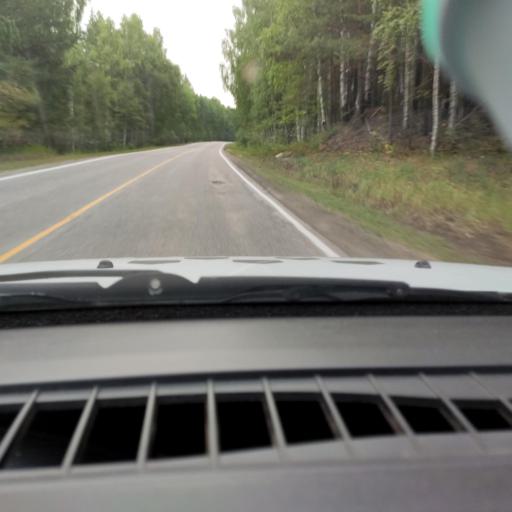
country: RU
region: Chelyabinsk
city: Ozersk
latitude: 55.8344
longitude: 60.6483
